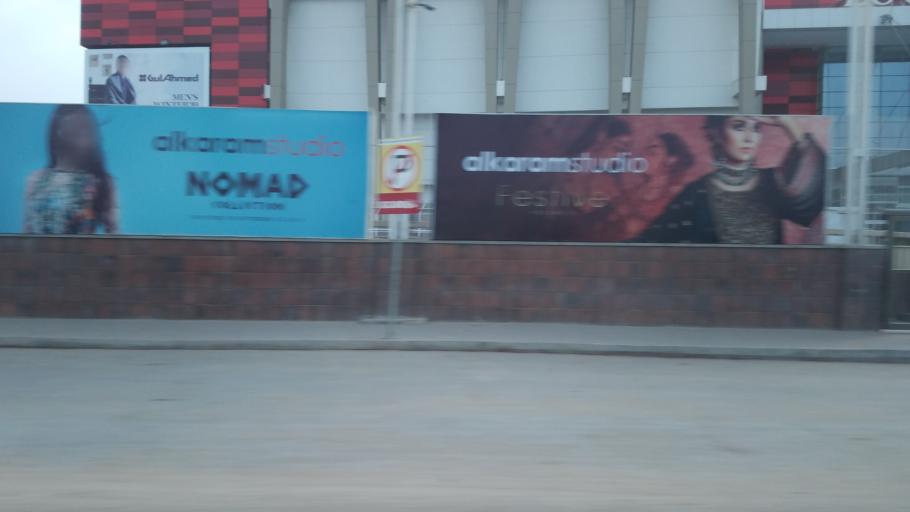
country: PK
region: Sindh
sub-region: Karachi District
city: Karachi
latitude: 24.9328
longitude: 67.0859
